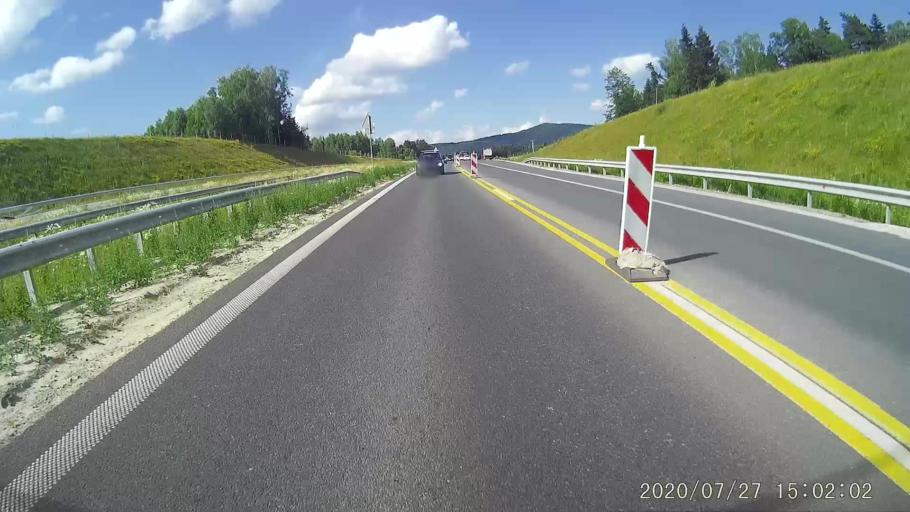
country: PL
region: Lesser Poland Voivodeship
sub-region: Powiat suski
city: Letownia
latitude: 49.6759
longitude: 19.8880
